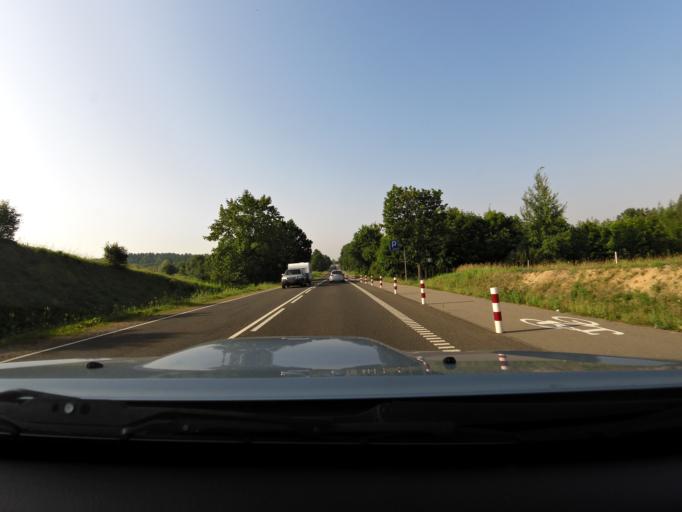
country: LT
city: Lazdijai
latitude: 54.1519
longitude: 23.4705
